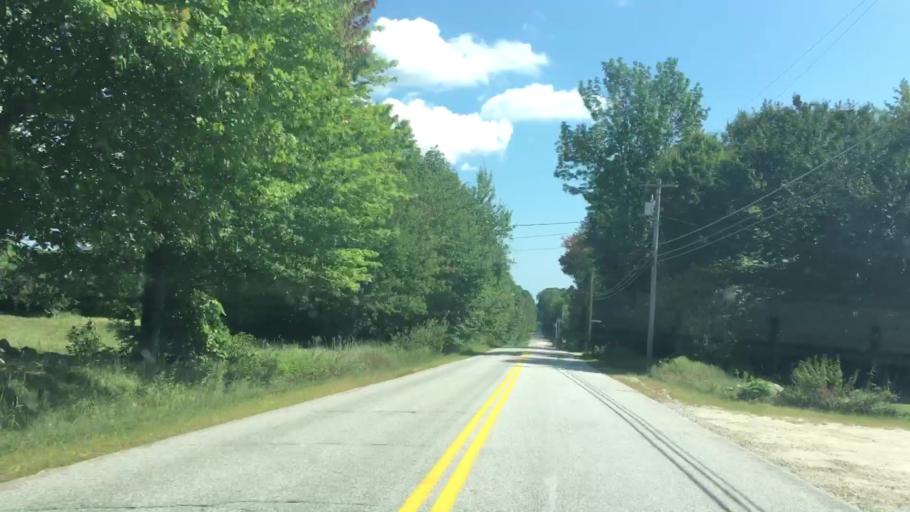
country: US
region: Maine
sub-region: Cumberland County
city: New Gloucester
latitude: 43.9413
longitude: -70.2978
